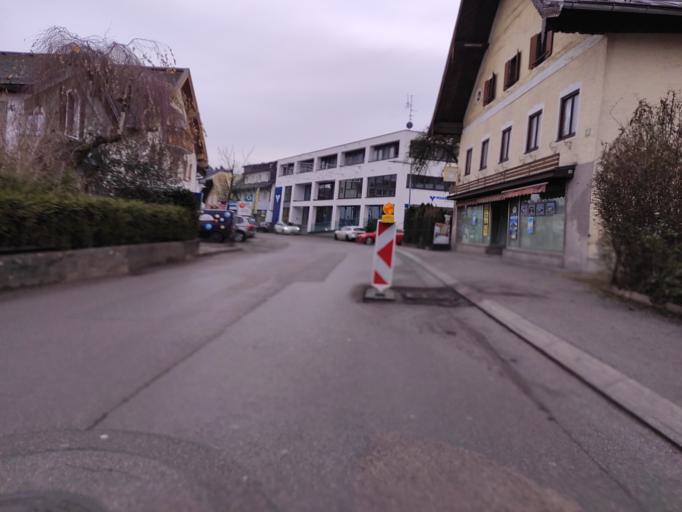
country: AT
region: Salzburg
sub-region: Politischer Bezirk Salzburg-Umgebung
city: Seekirchen am Wallersee
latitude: 47.8952
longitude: 13.1243
